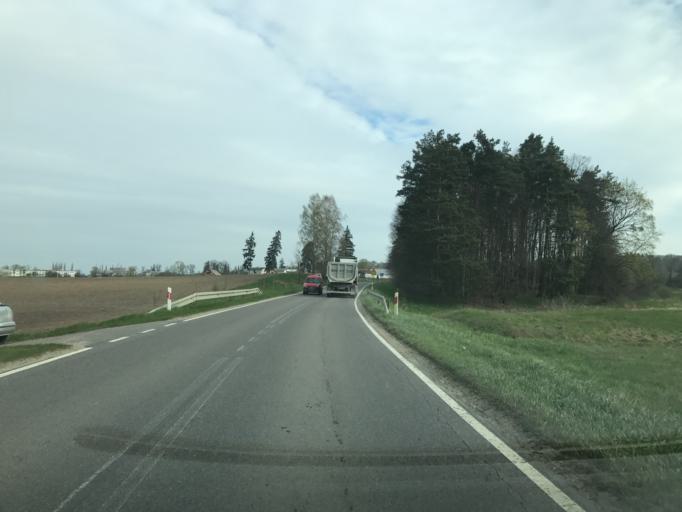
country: PL
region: Warmian-Masurian Voivodeship
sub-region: Powiat ostrodzki
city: Gierzwald
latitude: 53.5340
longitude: 20.0876
